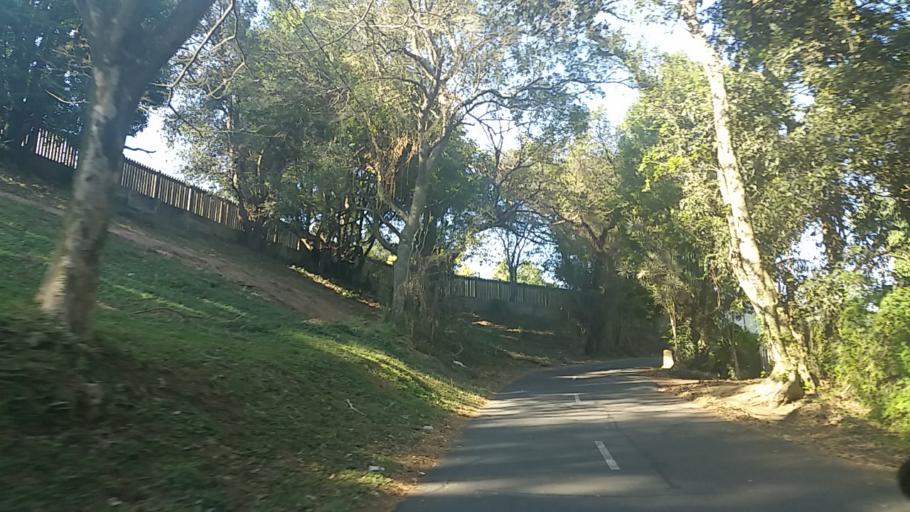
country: ZA
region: KwaZulu-Natal
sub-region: eThekwini Metropolitan Municipality
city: Berea
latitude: -29.8406
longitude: 30.9188
